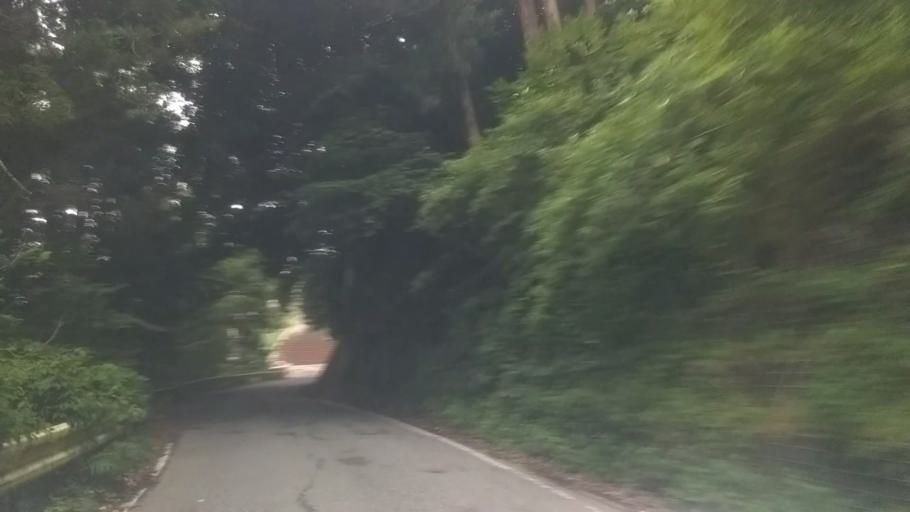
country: JP
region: Chiba
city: Kawaguchi
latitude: 35.1393
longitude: 140.1502
